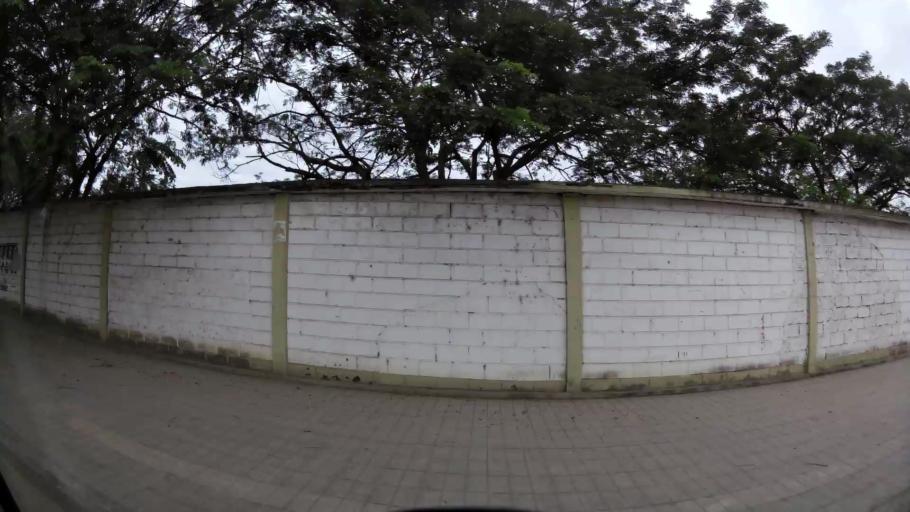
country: EC
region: El Oro
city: Machala
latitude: -3.2601
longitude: -79.9417
